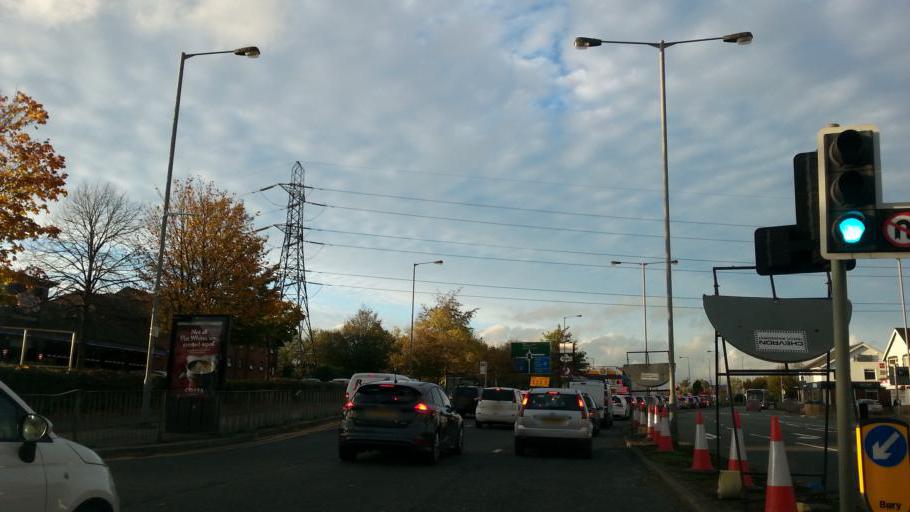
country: GB
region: England
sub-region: Borough of Bury
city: Prestwich
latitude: 53.5366
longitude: -2.2880
